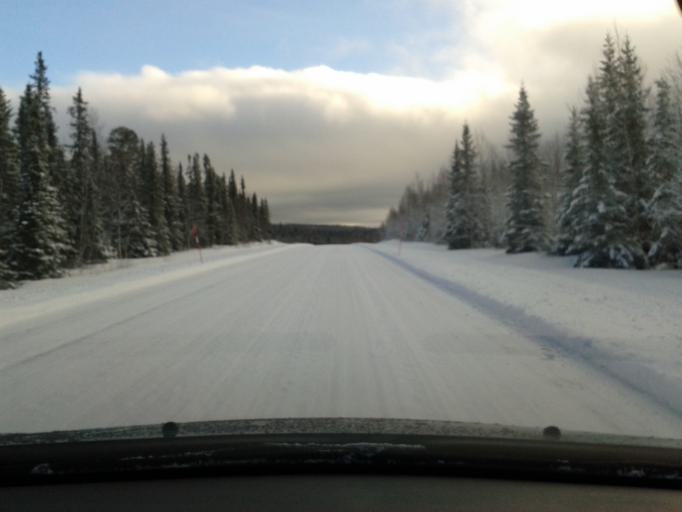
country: SE
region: Vaesterbotten
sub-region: Vilhelmina Kommun
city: Sjoberg
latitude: 65.2580
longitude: 15.6844
